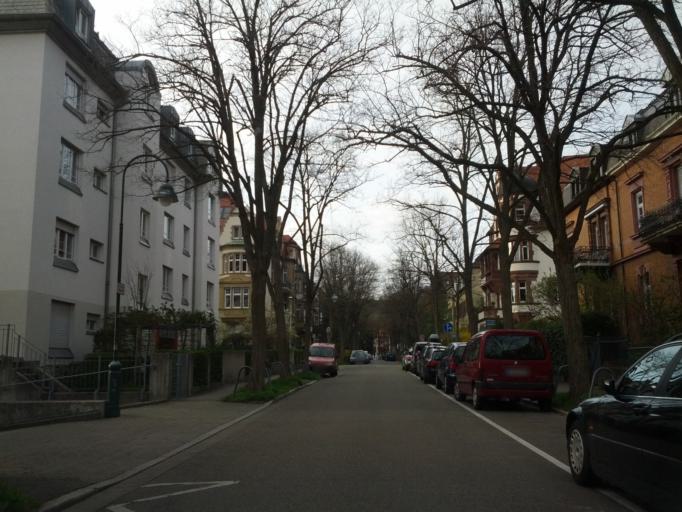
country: DE
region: Baden-Wuerttemberg
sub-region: Freiburg Region
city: Freiburg
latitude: 47.9853
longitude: 7.8602
